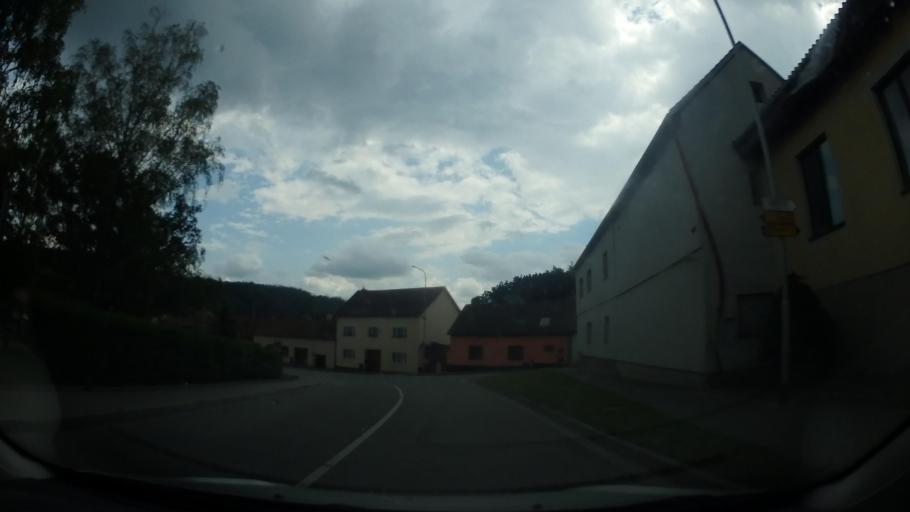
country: CZ
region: South Moravian
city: Svitavka
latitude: 49.4802
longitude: 16.6049
